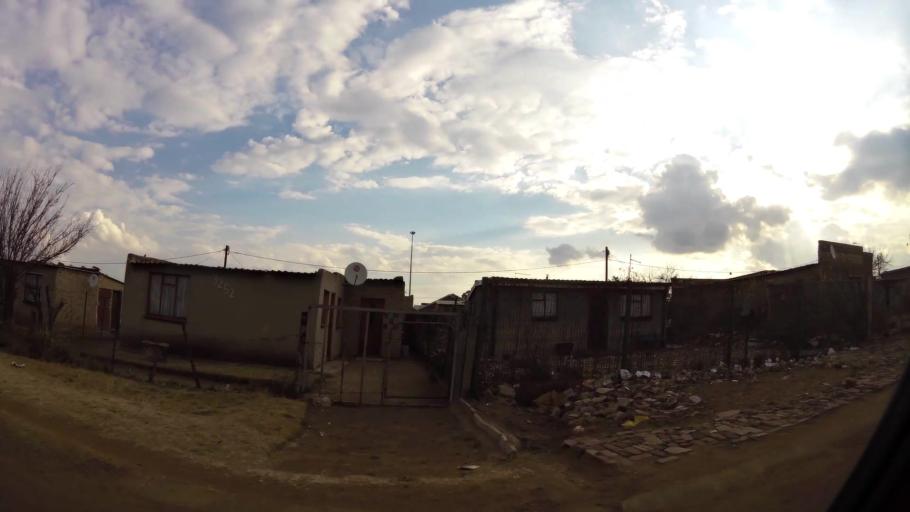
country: ZA
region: Gauteng
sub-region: Sedibeng District Municipality
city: Vanderbijlpark
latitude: -26.6690
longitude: 27.8673
